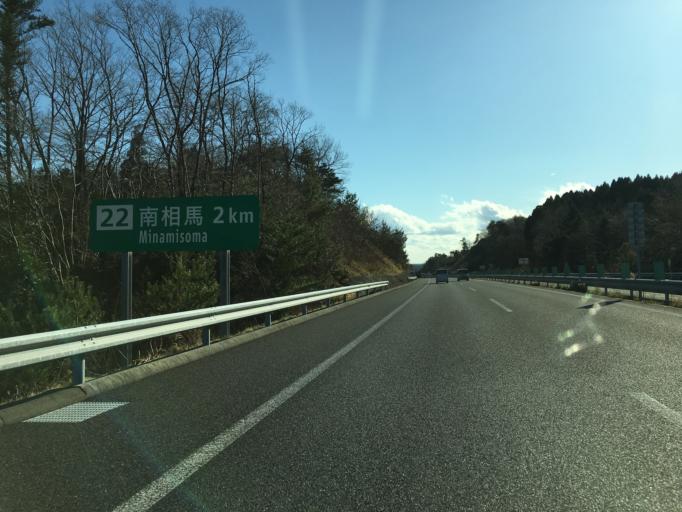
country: JP
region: Fukushima
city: Namie
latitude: 37.6776
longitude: 140.9176
